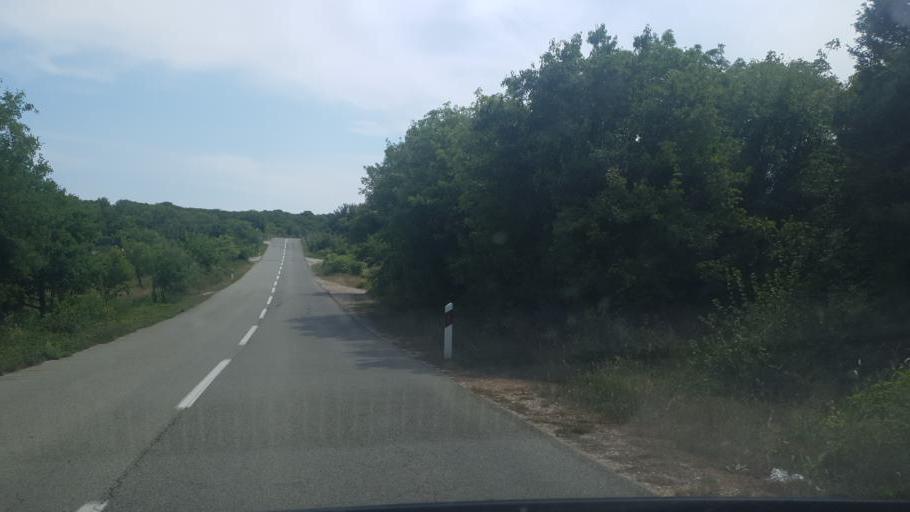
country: HR
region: Primorsko-Goranska
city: Punat
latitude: 45.0550
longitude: 14.6496
